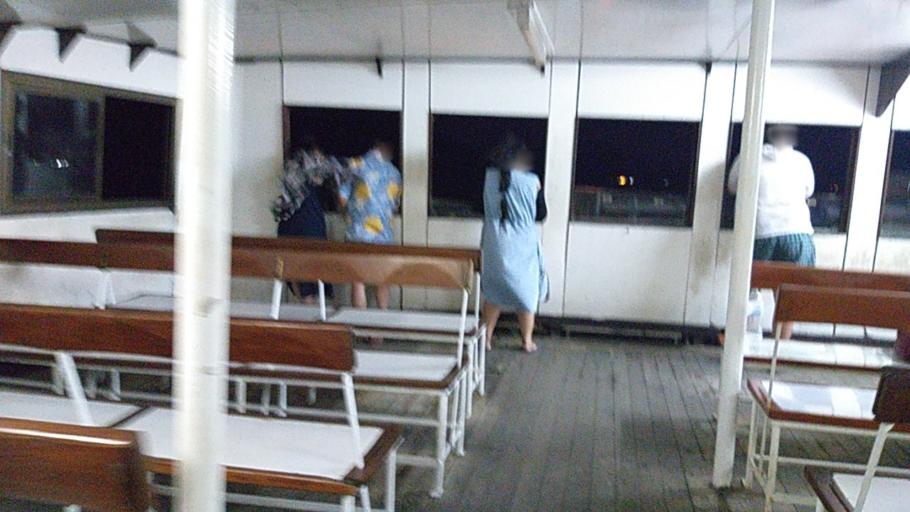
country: TH
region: Trat
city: Laem Ngop
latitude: 12.1741
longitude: 102.2980
